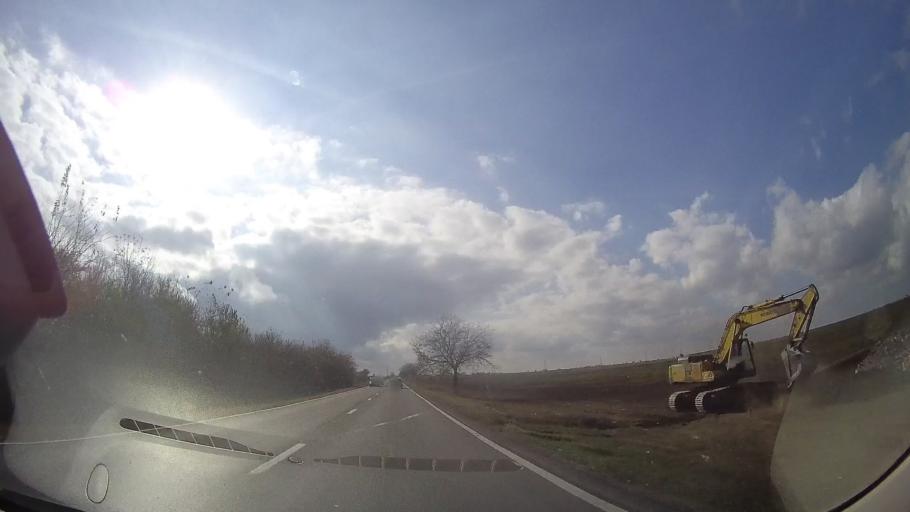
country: RO
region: Constanta
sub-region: Comuna Agigea
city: Agigea
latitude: 44.0811
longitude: 28.6042
